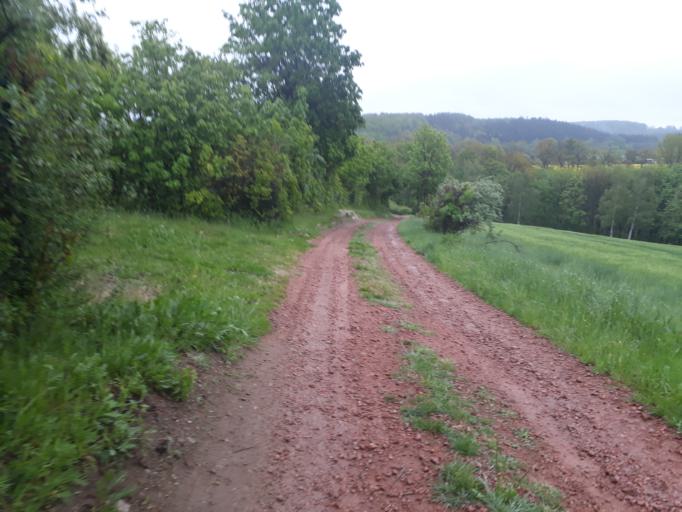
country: DE
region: Saxony
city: Reinhardtsgrimma
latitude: 50.8903
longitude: 13.7417
